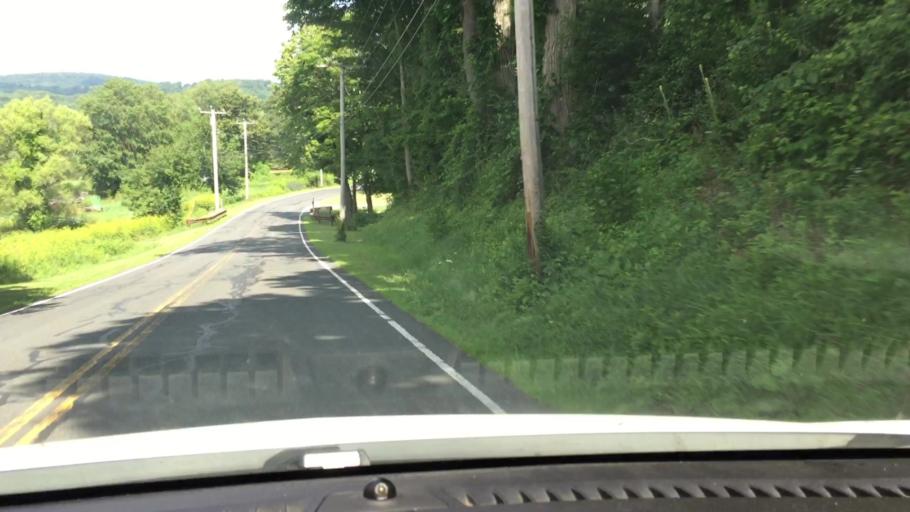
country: US
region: Massachusetts
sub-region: Berkshire County
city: Lee
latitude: 42.2298
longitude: -73.1927
